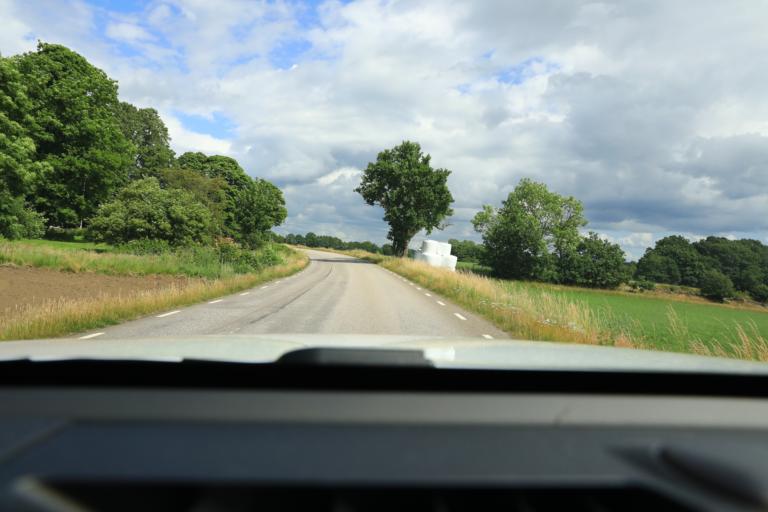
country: SE
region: Halland
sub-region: Varbergs Kommun
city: Tvaaker
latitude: 57.0874
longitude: 12.4064
